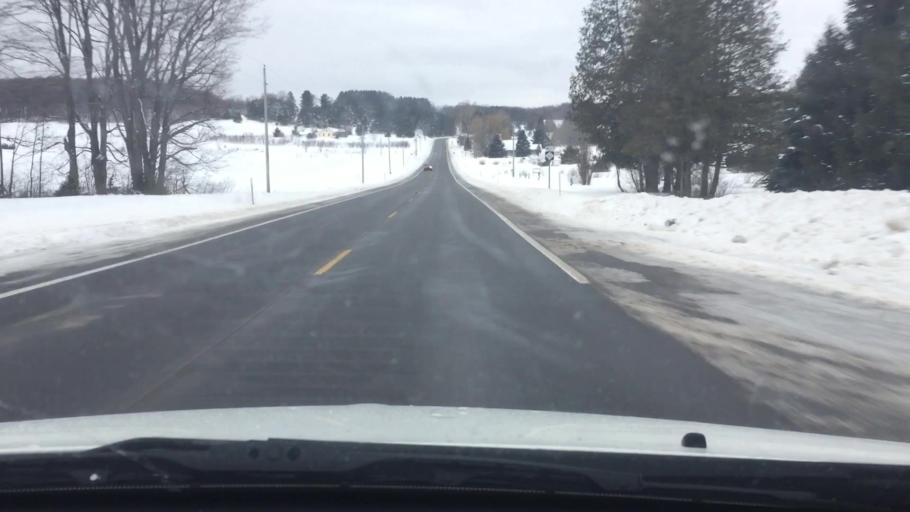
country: US
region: Michigan
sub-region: Charlevoix County
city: East Jordan
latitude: 45.1035
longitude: -85.0404
